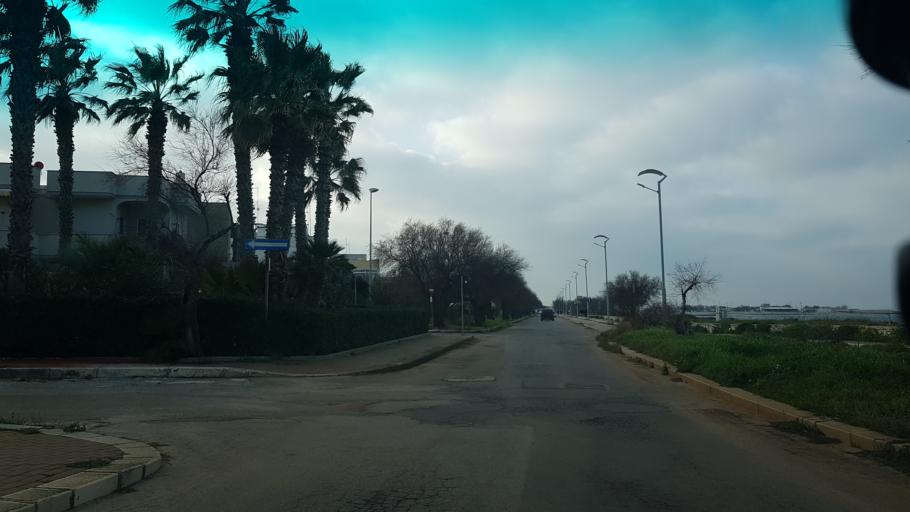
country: IT
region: Apulia
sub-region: Provincia di Brindisi
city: Carovigno
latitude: 40.7394
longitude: 17.7403
